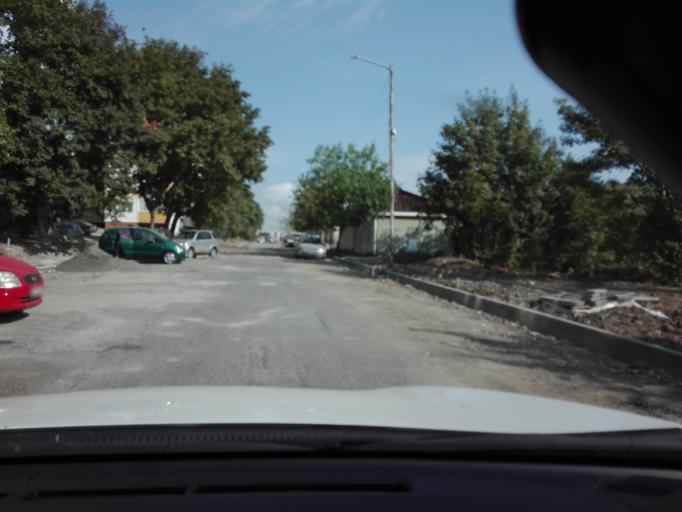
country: BG
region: Burgas
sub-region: Obshtina Burgas
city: Burgas
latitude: 42.4490
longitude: 27.4130
